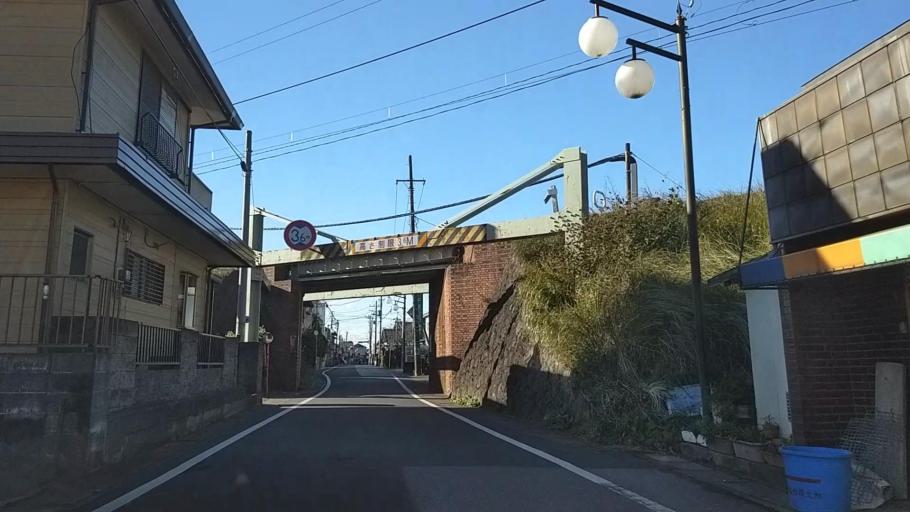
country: JP
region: Chiba
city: Futtsu
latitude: 35.2846
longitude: 139.8578
